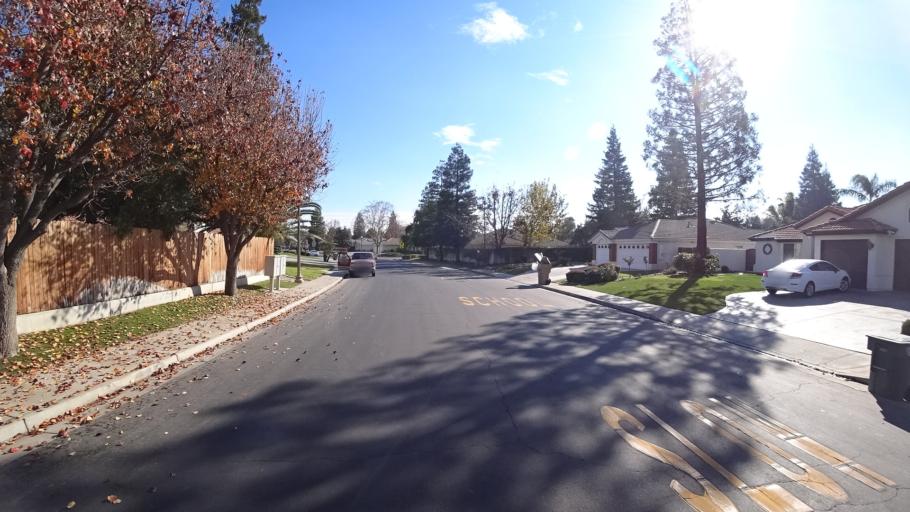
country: US
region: California
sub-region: Kern County
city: Greenacres
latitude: 35.3479
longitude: -119.1213
